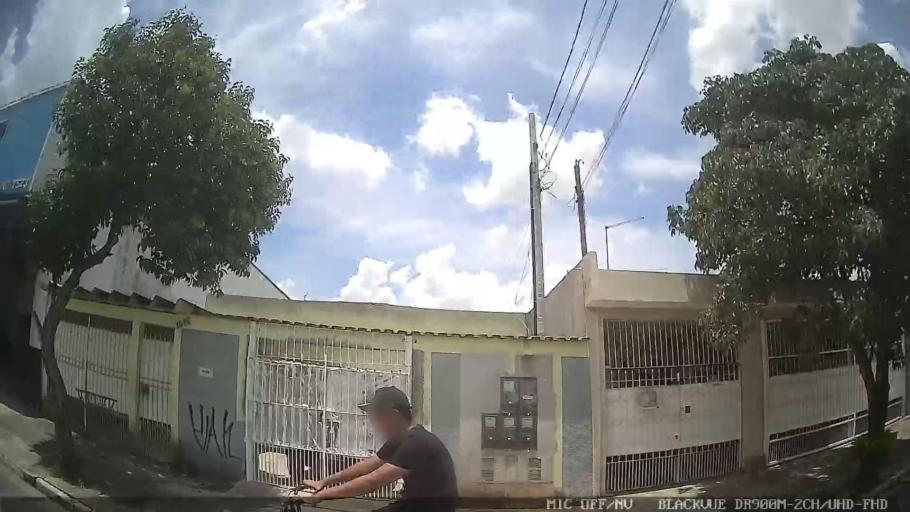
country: BR
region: Sao Paulo
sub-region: Suzano
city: Suzano
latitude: -23.5393
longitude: -46.3224
